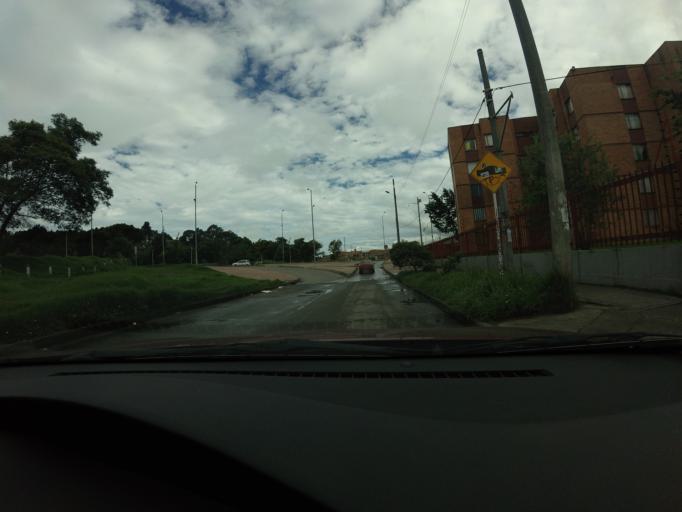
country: CO
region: Cundinamarca
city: Soacha
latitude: 4.6079
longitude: -74.1611
